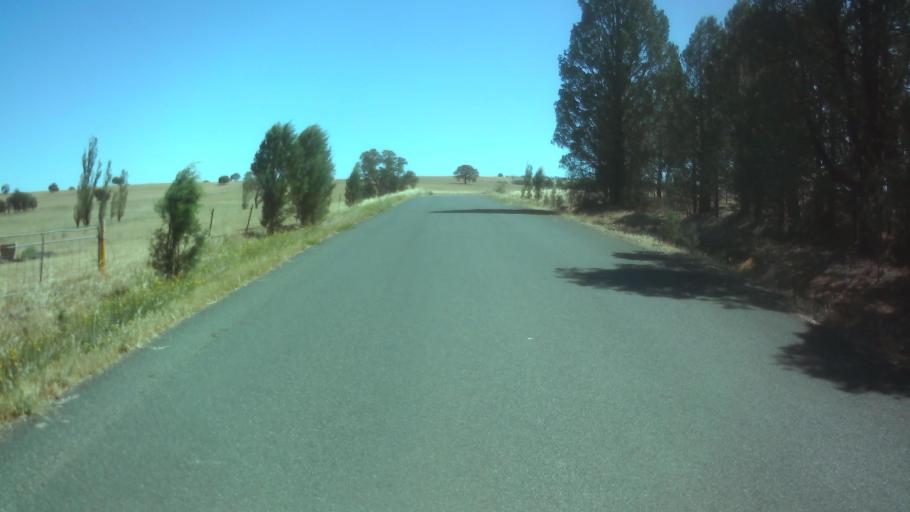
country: AU
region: New South Wales
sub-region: Weddin
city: Grenfell
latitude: -33.9788
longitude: 148.4021
